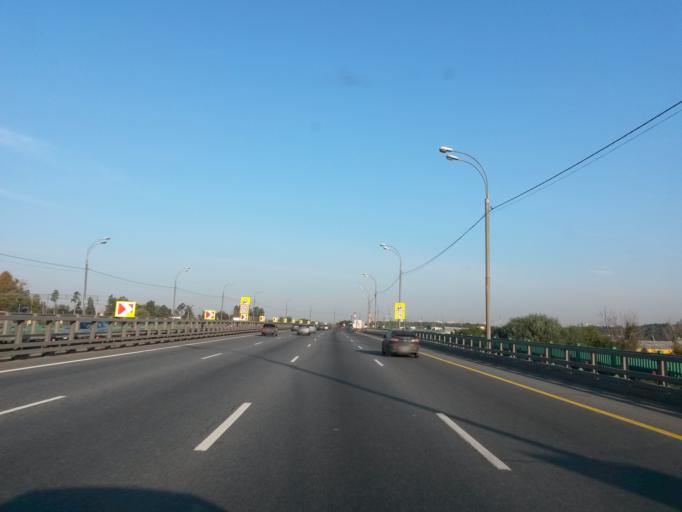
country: RU
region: Moskovskaya
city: Vidnoye
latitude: 55.5488
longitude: 37.6873
